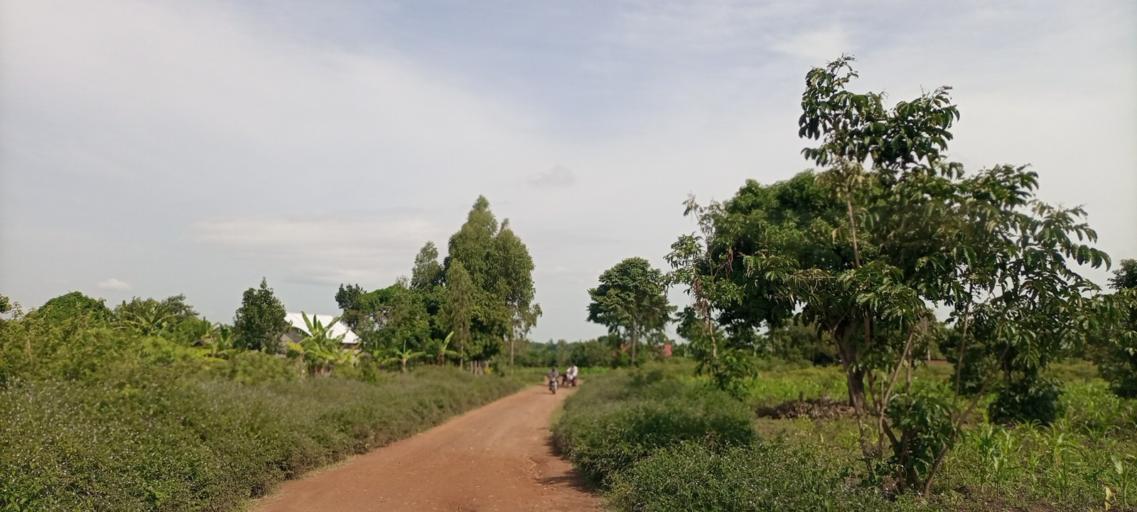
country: UG
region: Eastern Region
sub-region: Mbale District
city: Mbale
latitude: 1.1291
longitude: 34.0388
